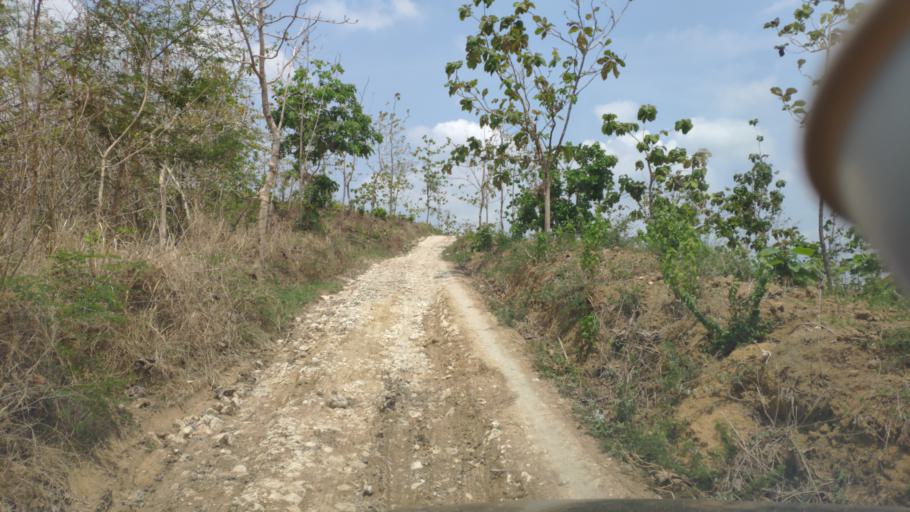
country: ID
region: Central Java
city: Gumiring
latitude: -7.0519
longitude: 111.4009
